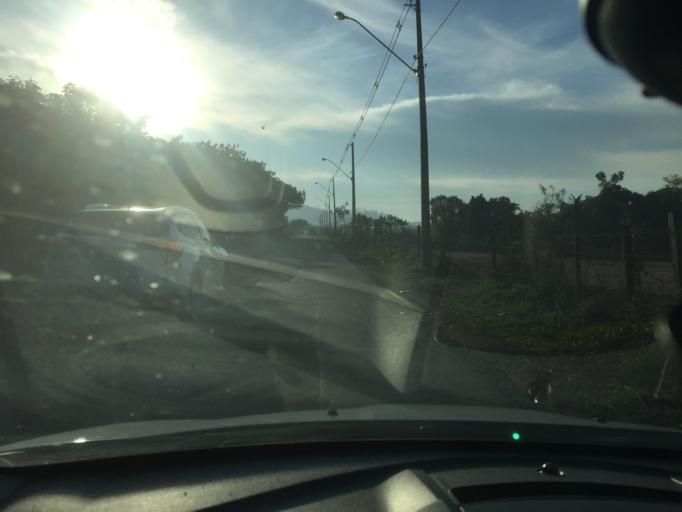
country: BR
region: Sao Paulo
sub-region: Varzea Paulista
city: Varzea Paulista
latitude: -23.2028
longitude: -46.8567
